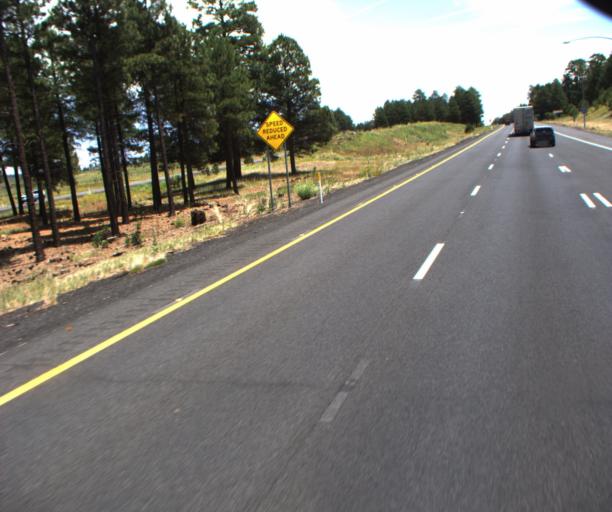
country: US
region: Arizona
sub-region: Coconino County
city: Flagstaff
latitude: 35.1836
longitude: -111.7042
